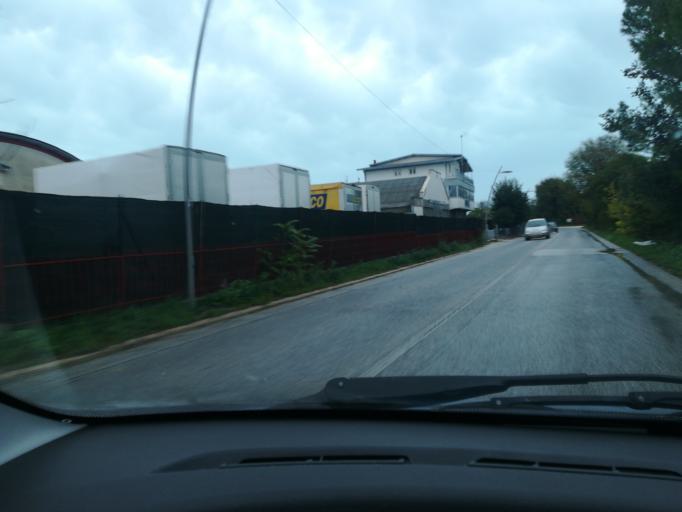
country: IT
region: The Marches
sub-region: Provincia di Macerata
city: Trodica
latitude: 43.2755
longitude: 13.5991
